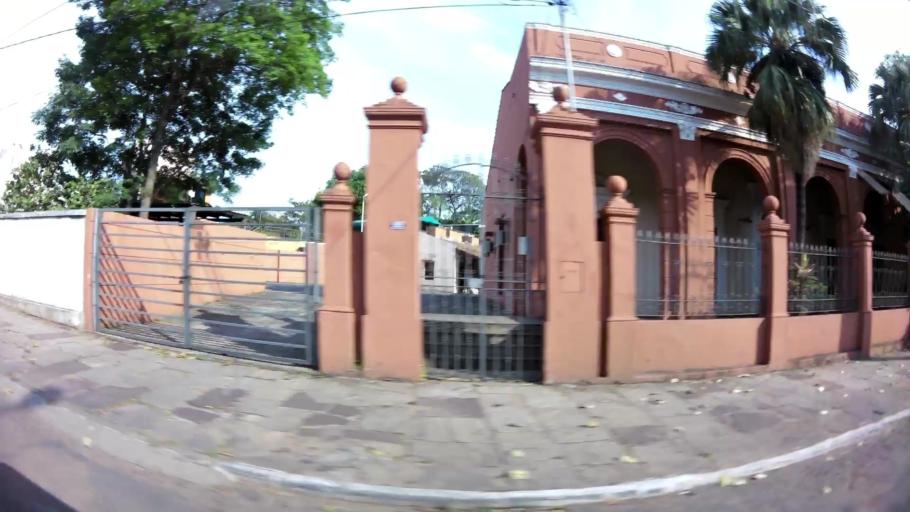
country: PY
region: Asuncion
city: Asuncion
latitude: -25.2837
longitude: -57.6210
